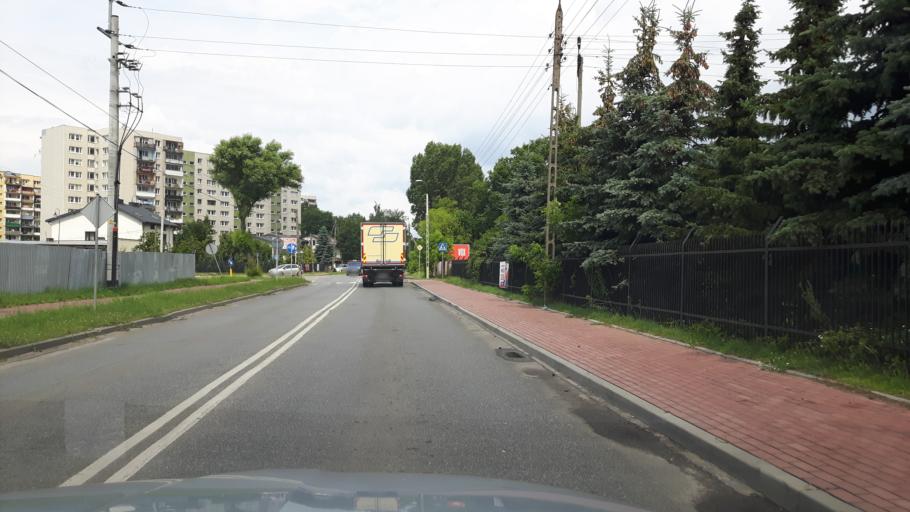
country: PL
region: Masovian Voivodeship
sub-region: Powiat wolominski
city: Nowe Lipiny
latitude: 52.3491
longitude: 21.2643
